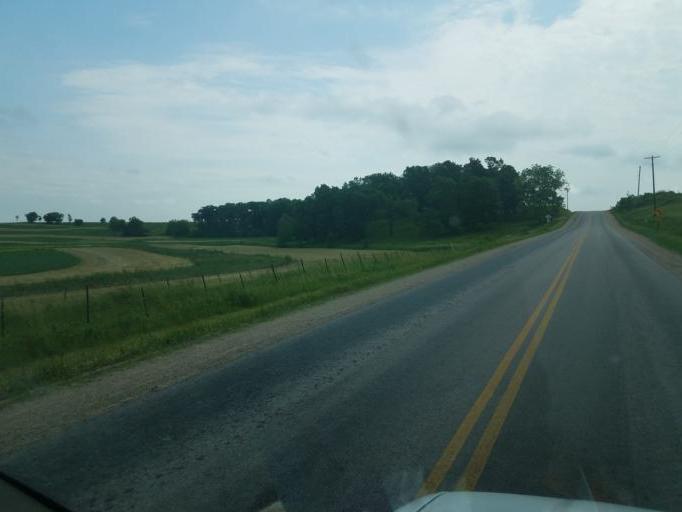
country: US
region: Wisconsin
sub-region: Monroe County
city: Cashton
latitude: 43.7548
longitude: -90.7547
